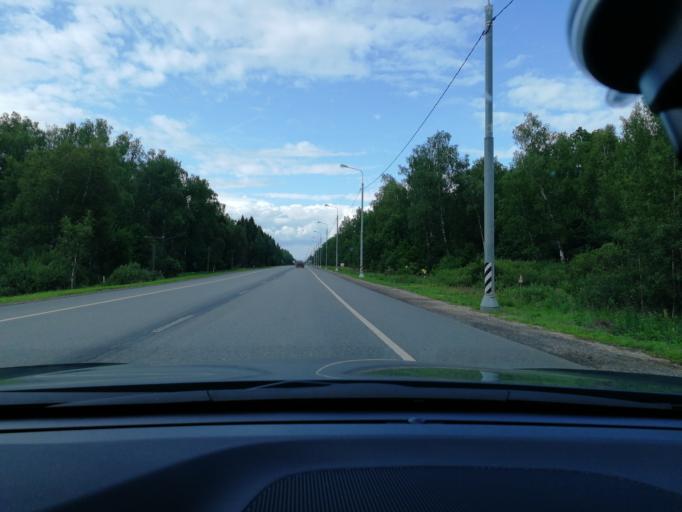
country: RU
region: Moskovskaya
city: Proletarskiy
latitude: 55.0522
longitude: 37.4331
